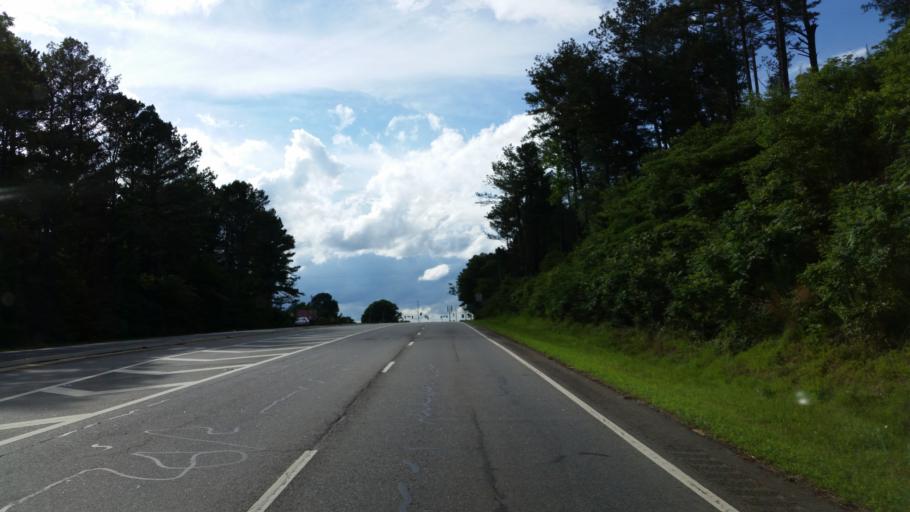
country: US
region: Georgia
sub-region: Bartow County
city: Cartersville
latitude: 34.1561
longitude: -84.7839
